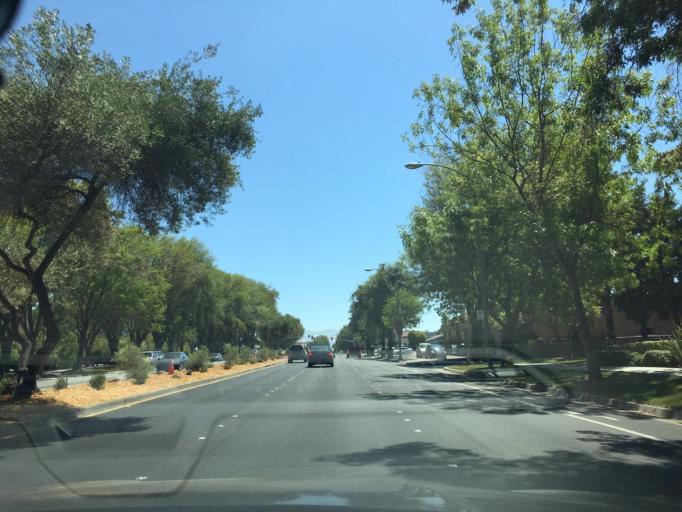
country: US
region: California
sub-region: Santa Clara County
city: Cupertino
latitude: 37.3229
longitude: -122.0170
